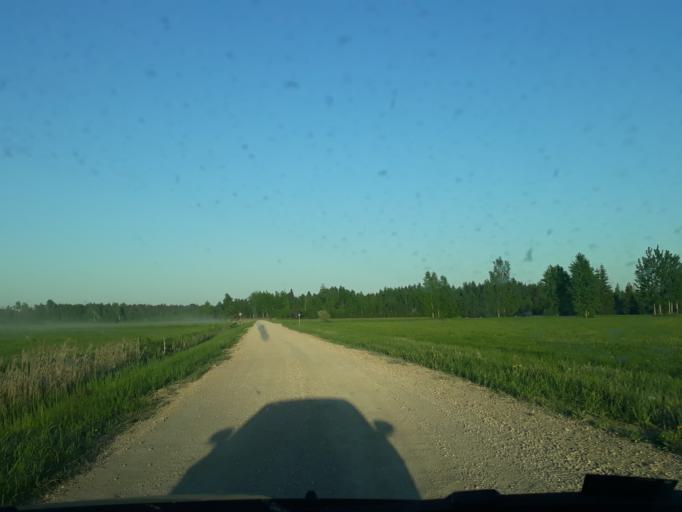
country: EE
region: Paernumaa
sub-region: Tootsi vald
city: Tootsi
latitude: 58.5812
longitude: 24.9080
